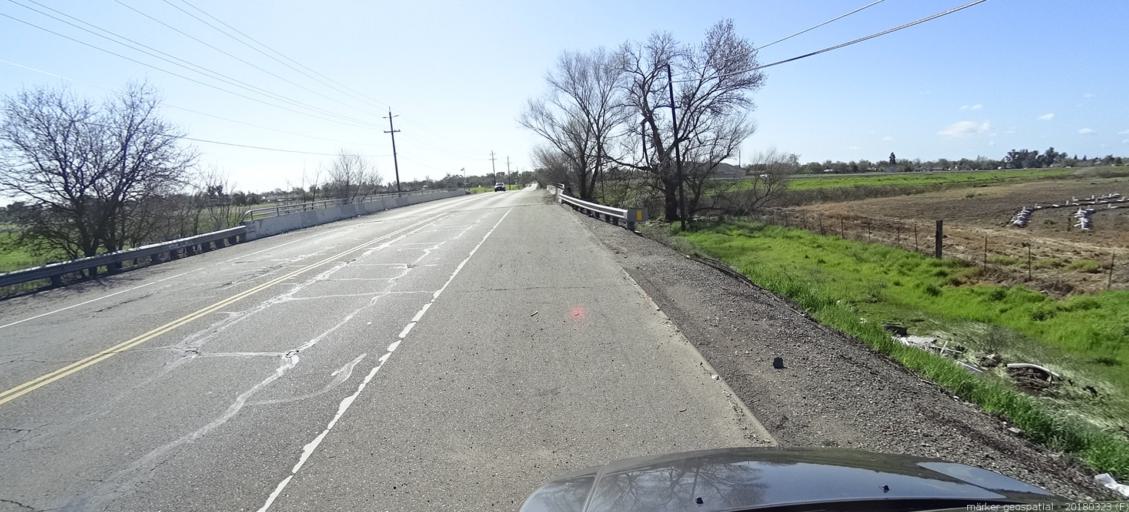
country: US
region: California
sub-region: Sacramento County
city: Rio Linda
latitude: 38.6676
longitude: -121.4518
